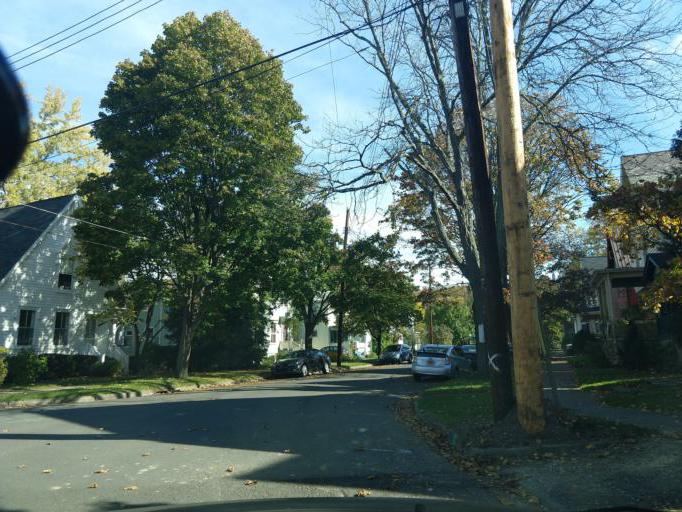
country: US
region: New York
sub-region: Tompkins County
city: Ithaca
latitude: 42.4471
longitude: -76.5007
